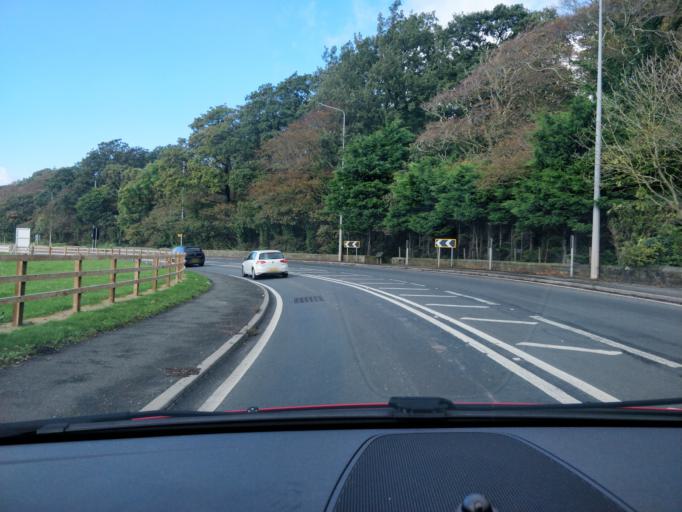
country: GB
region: England
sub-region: Lancashire
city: Ormskirk
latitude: 53.6006
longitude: -2.9269
